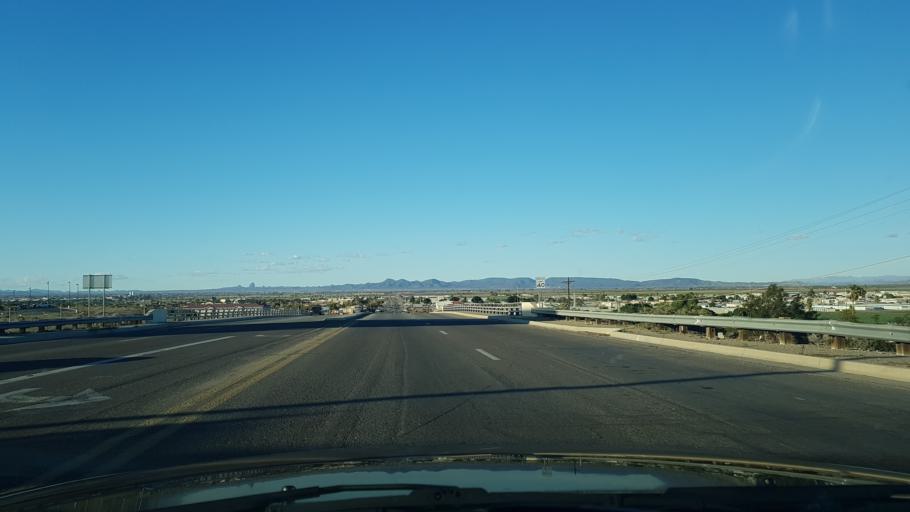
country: US
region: Arizona
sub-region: Yuma County
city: Yuma
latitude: 32.6914
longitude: -114.5988
